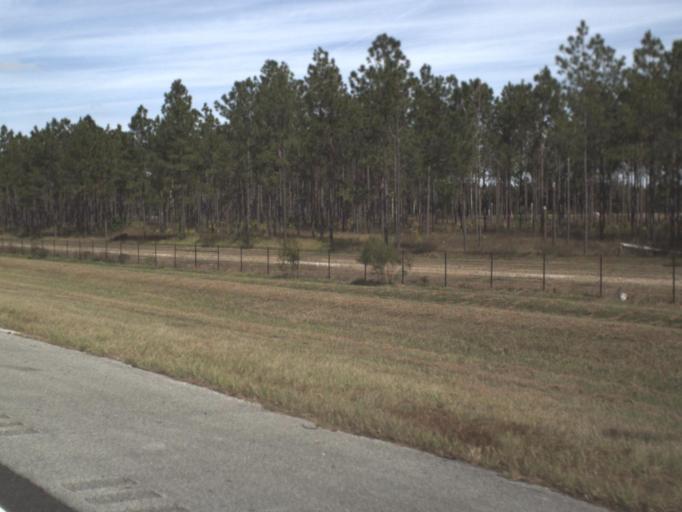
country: US
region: Florida
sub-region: Polk County
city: Citrus Ridge
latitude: 28.3914
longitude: -81.6180
